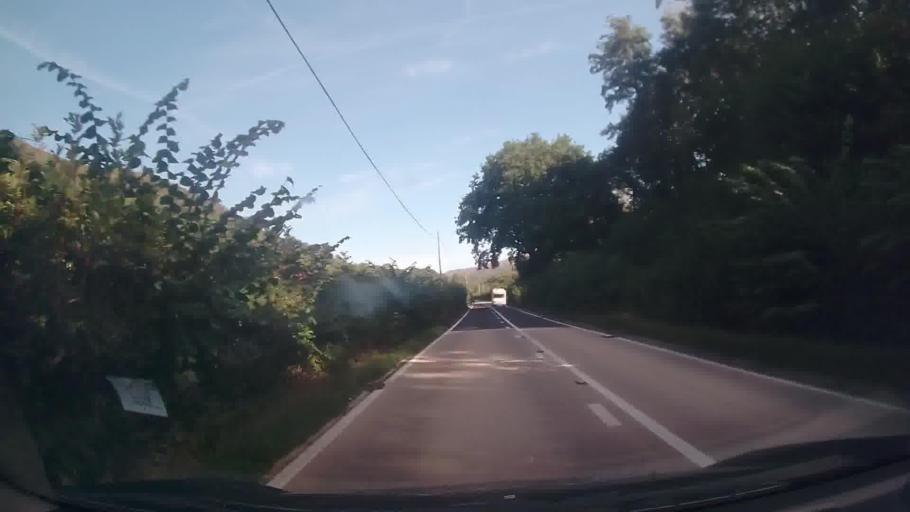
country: GB
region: Wales
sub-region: Blaenau Gwent
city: Brynmawr
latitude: 51.9119
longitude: -3.1920
